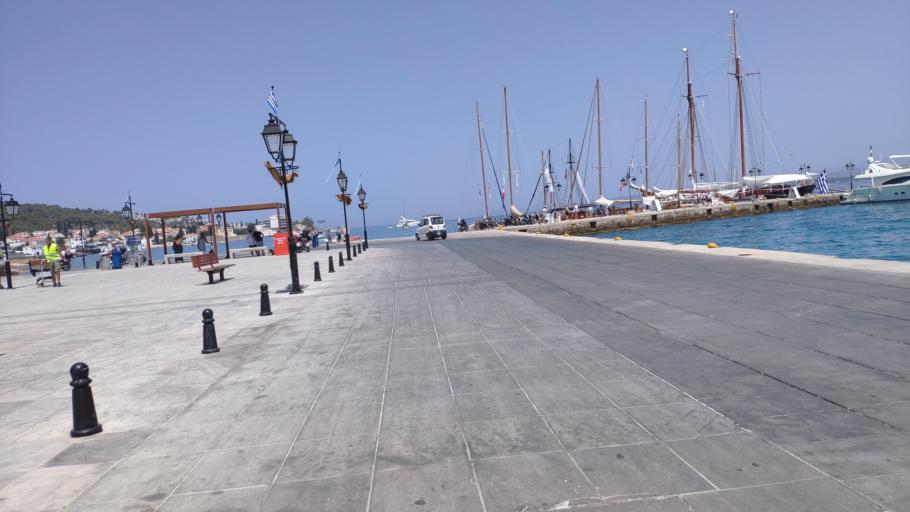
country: GR
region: Attica
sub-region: Nomos Piraios
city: Spetses
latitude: 37.2690
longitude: 23.1551
